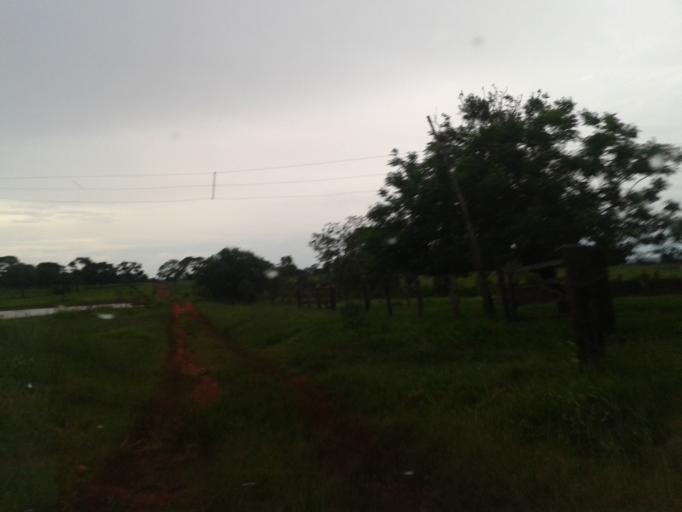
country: BR
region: Minas Gerais
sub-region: Santa Vitoria
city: Santa Vitoria
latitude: -19.2294
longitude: -50.5056
